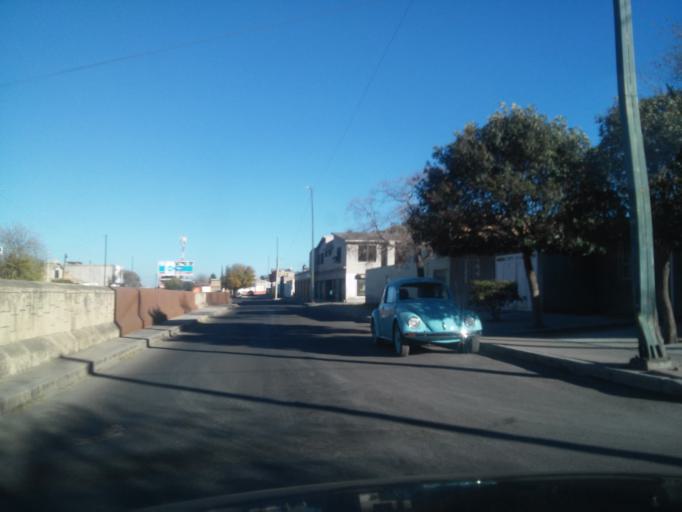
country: MX
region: Durango
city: Victoria de Durango
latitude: 24.0156
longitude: -104.6402
